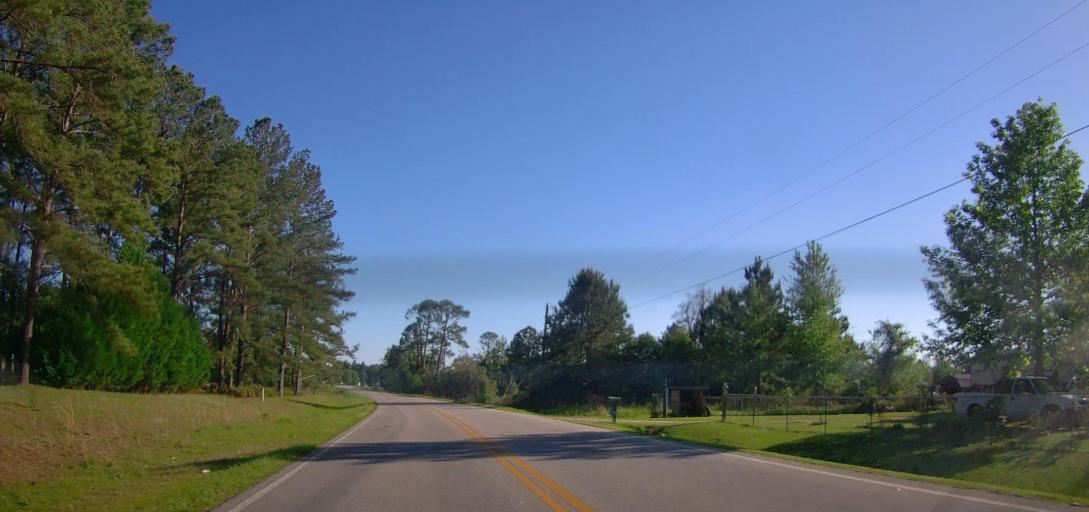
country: US
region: Georgia
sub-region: Ben Hill County
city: Fitzgerald
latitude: 31.7353
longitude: -83.2354
